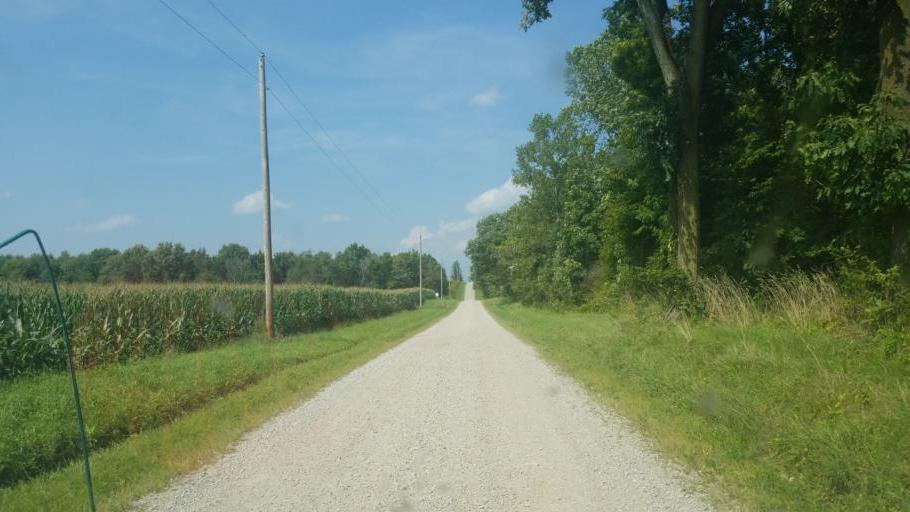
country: US
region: Ohio
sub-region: Huron County
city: New London
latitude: 41.0612
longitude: -82.4099
